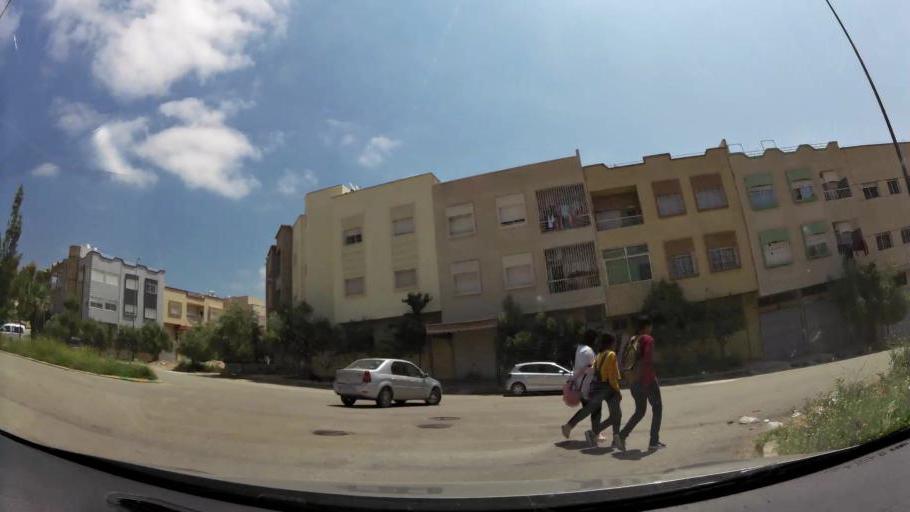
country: MA
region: Fes-Boulemane
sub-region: Fes
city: Fes
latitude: 34.0627
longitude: -5.0252
